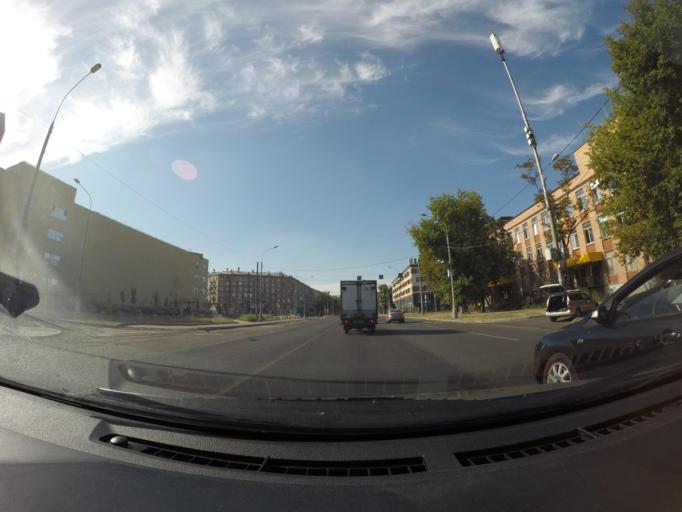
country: RU
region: Moscow
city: Mar'ina Roshcha
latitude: 55.8133
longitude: 37.6029
